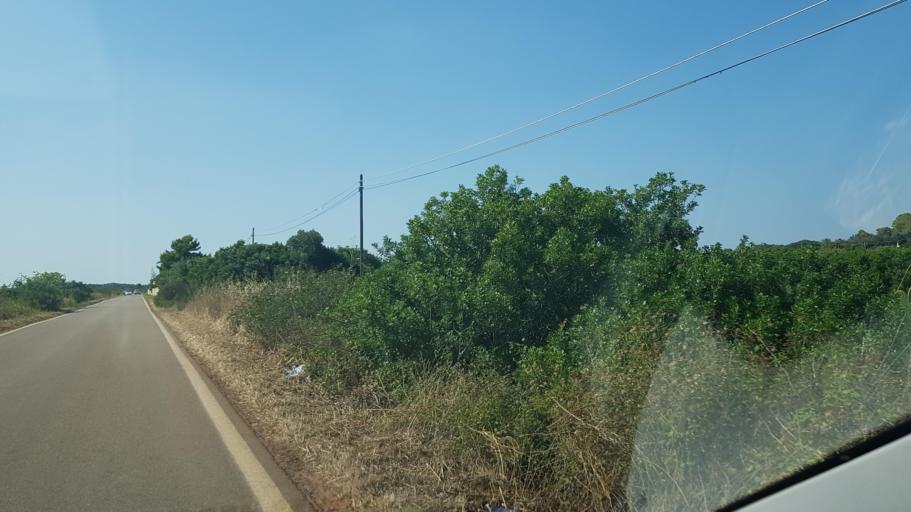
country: IT
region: Apulia
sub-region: Provincia di Lecce
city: Gemini
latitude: 39.8519
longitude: 18.2081
